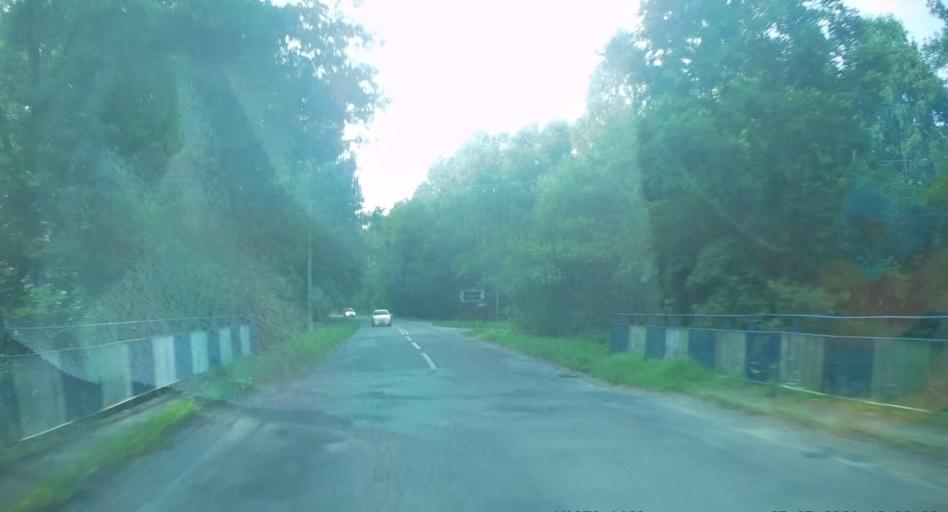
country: PL
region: Lodz Voivodeship
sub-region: Powiat opoczynski
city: Bialaczow
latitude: 51.3292
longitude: 20.3433
